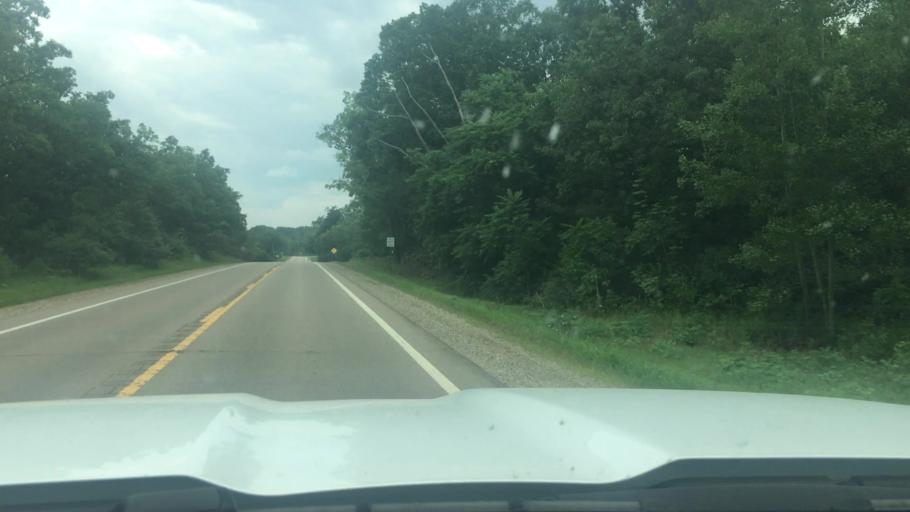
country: US
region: Michigan
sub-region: Ionia County
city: Portland
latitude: 43.0002
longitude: -84.9041
